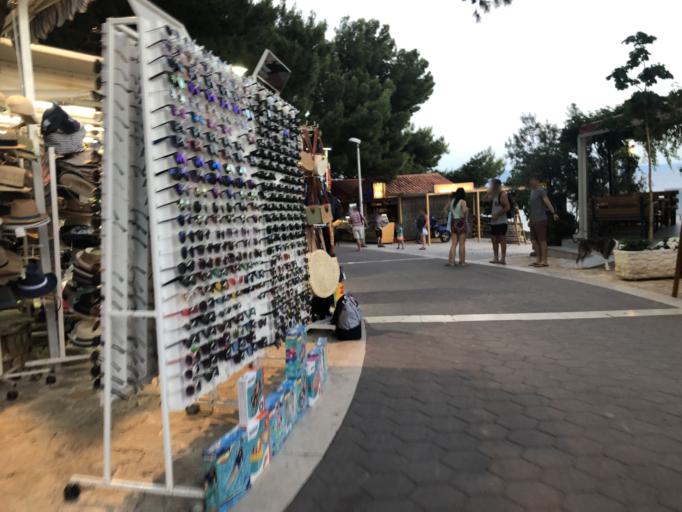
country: HR
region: Splitsko-Dalmatinska
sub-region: Grad Makarska
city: Makarska
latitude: 43.3058
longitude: 17.0027
